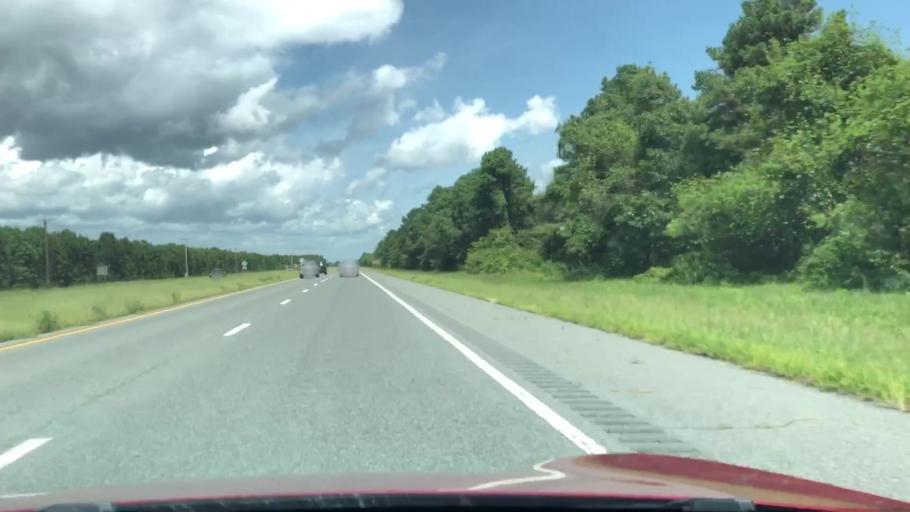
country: US
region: Virginia
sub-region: Northampton County
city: Cape Charles
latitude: 37.1566
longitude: -75.9710
